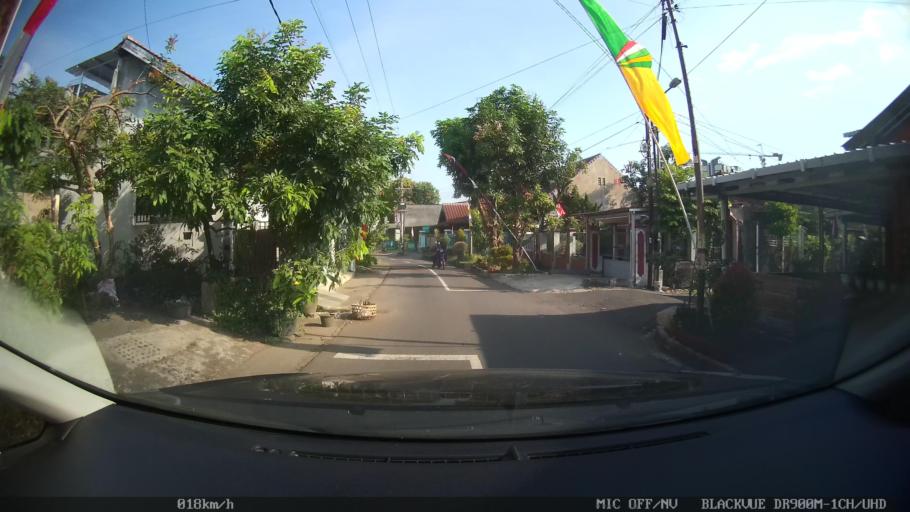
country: ID
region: Daerah Istimewa Yogyakarta
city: Yogyakarta
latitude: -7.8207
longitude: 110.3786
